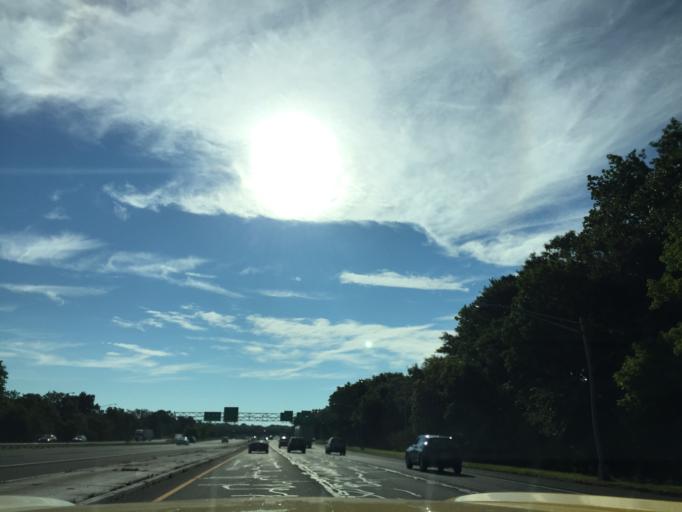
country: US
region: New Jersey
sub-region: Union County
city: Springfield
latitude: 40.7133
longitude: -74.3040
